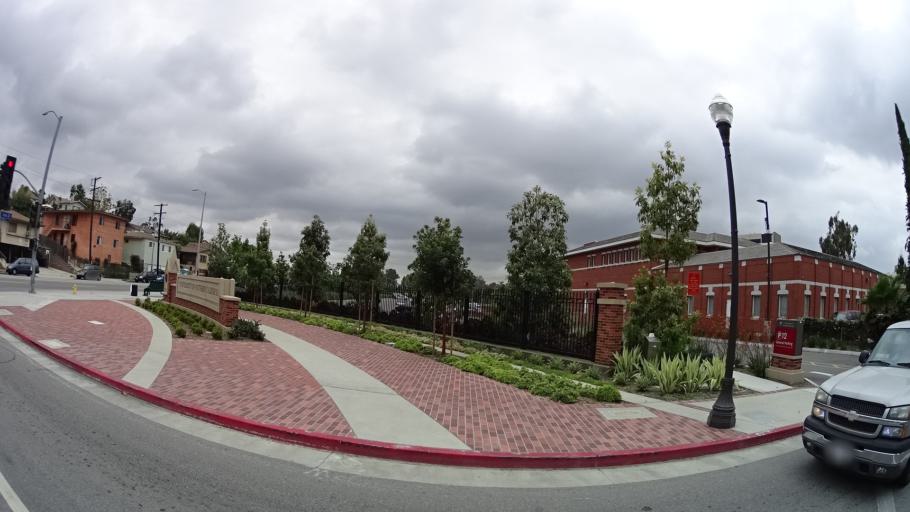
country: US
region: California
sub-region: Los Angeles County
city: Boyle Heights
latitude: 34.0624
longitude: -118.1984
